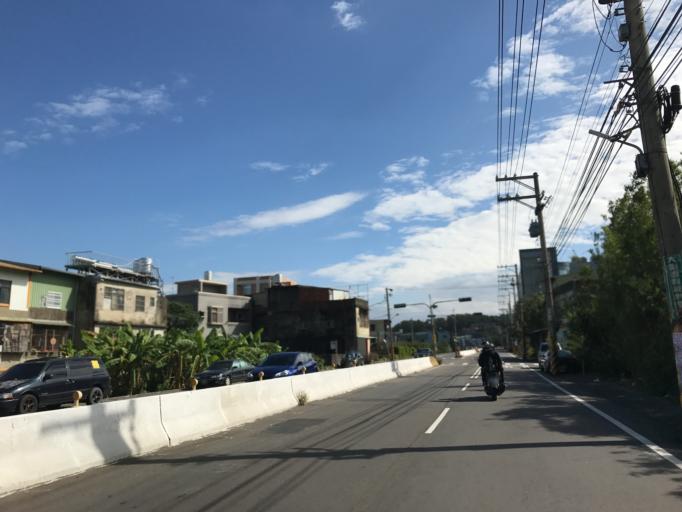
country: TW
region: Taiwan
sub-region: Hsinchu
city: Zhubei
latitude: 24.7773
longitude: 121.0339
